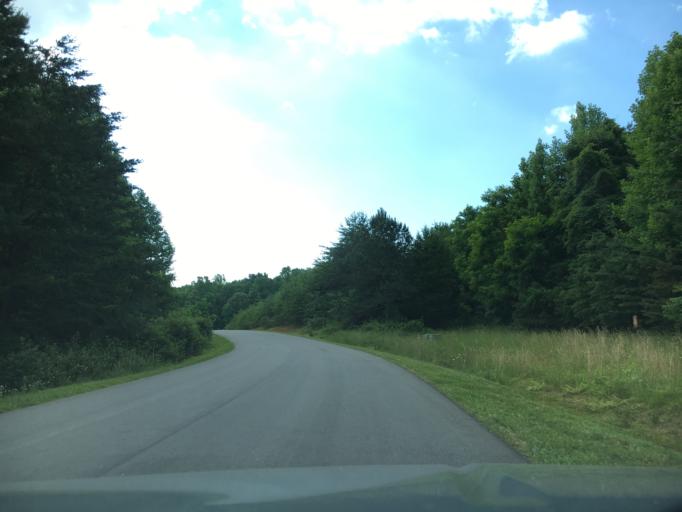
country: US
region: Virginia
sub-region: Bedford County
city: Forest
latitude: 37.3869
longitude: -79.2661
